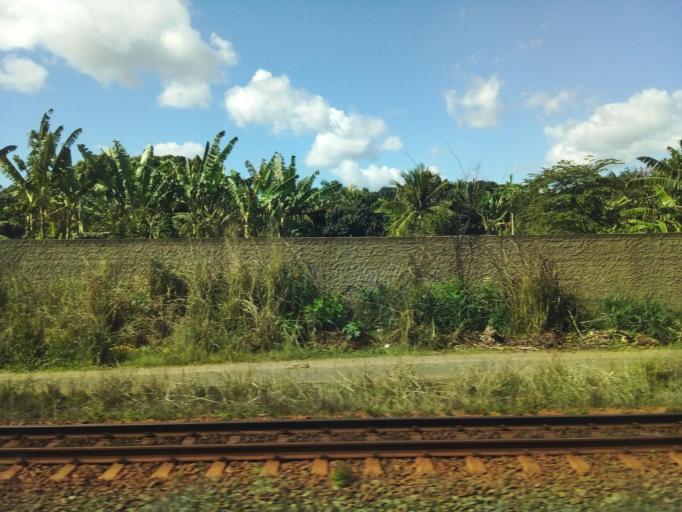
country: BR
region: Minas Gerais
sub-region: Governador Valadares
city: Governador Valadares
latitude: -18.8390
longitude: -41.8785
